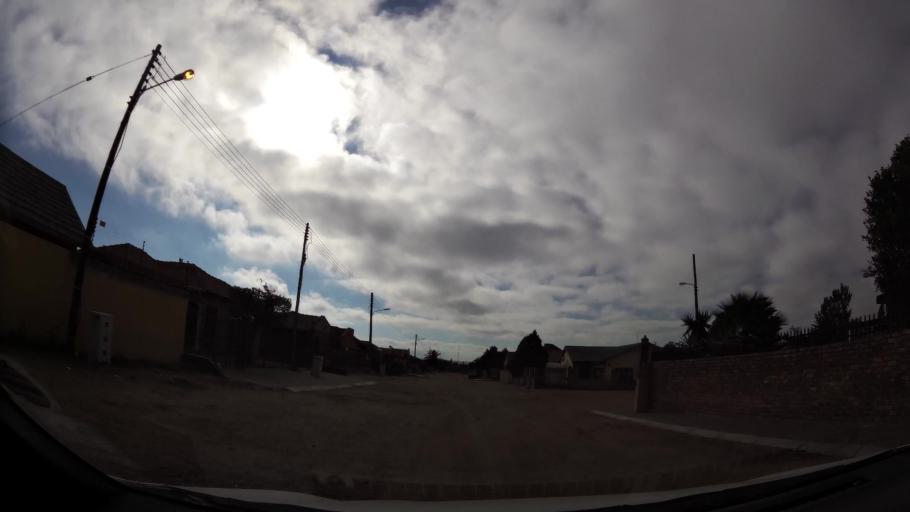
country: ZA
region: Limpopo
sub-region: Capricorn District Municipality
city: Polokwane
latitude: -23.8537
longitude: 29.3852
